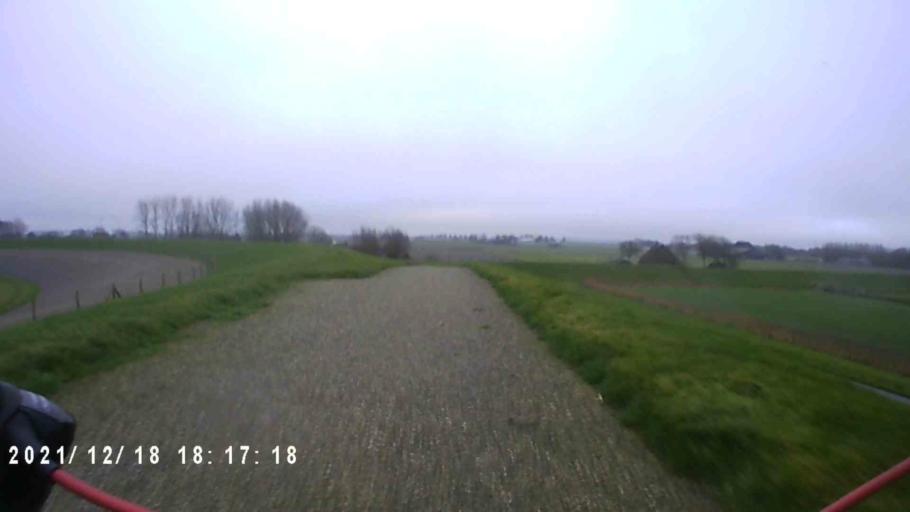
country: NL
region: Friesland
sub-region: Gemeente Dongeradeel
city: Ternaard
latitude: 53.3928
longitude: 5.9705
